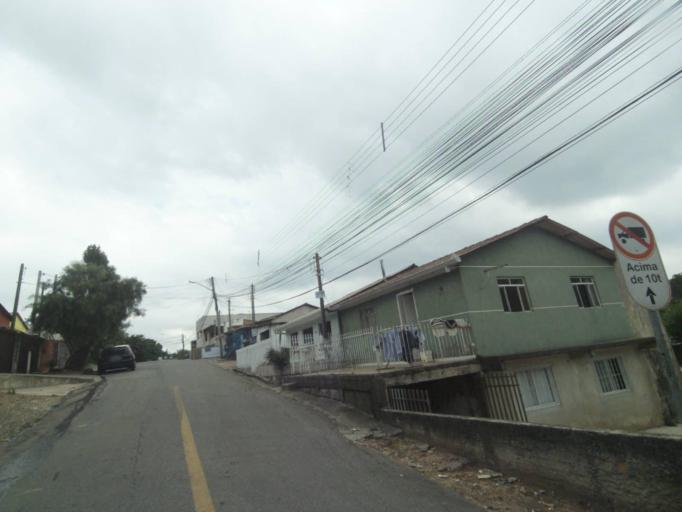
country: BR
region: Parana
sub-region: Curitiba
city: Curitiba
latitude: -25.4961
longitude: -49.3440
